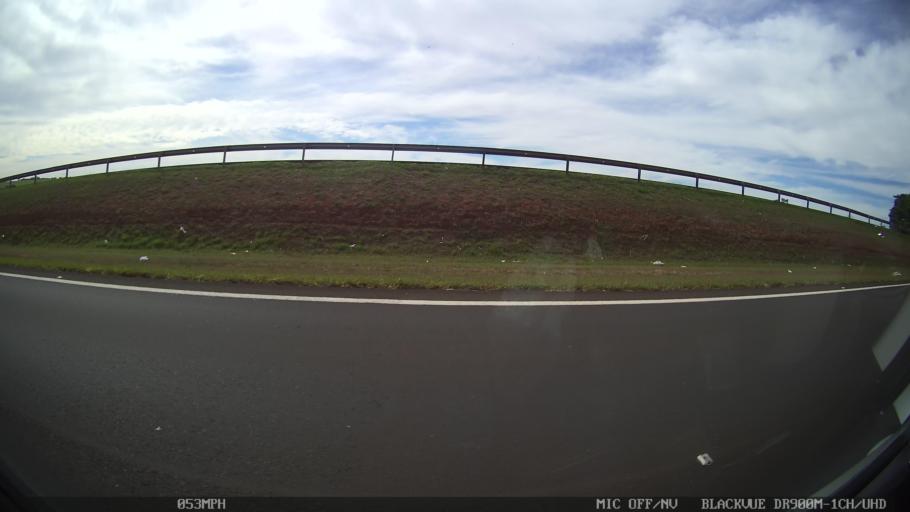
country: BR
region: Sao Paulo
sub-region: Taquaritinga
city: Taquaritinga
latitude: -21.5249
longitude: -48.5274
